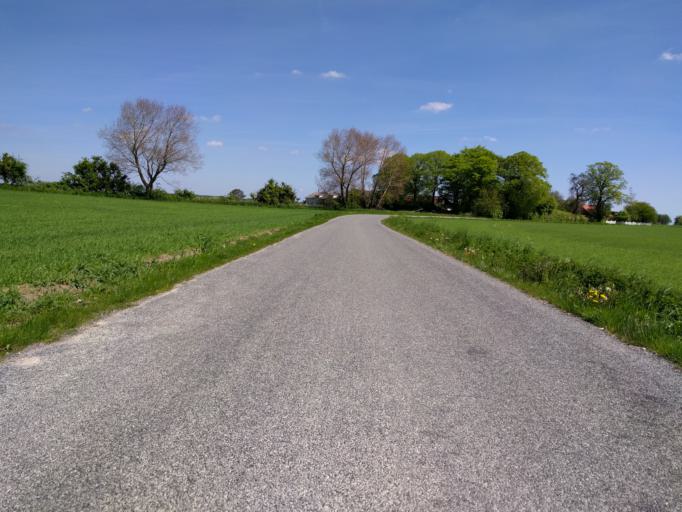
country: DK
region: Zealand
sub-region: Guldborgsund Kommune
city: Stubbekobing
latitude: 54.7447
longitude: 12.0194
